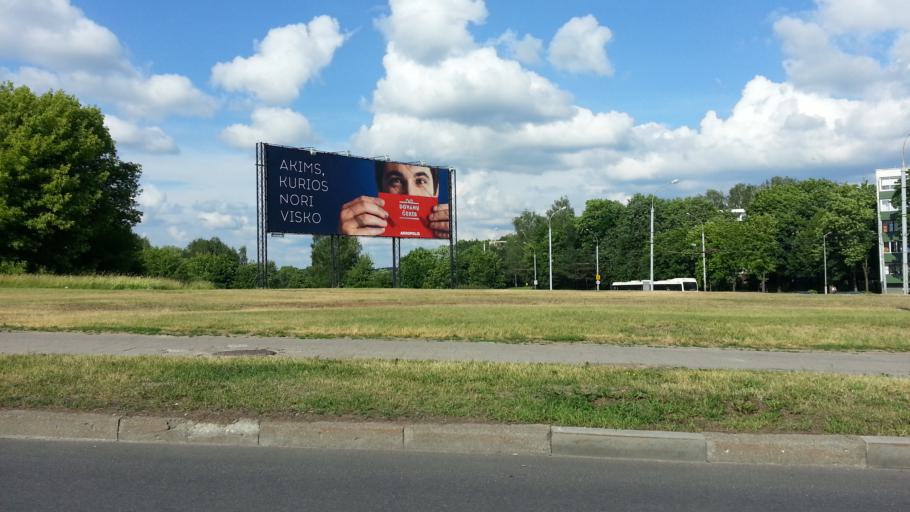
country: LT
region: Vilnius County
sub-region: Vilnius
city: Vilnius
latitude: 54.7208
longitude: 25.3022
